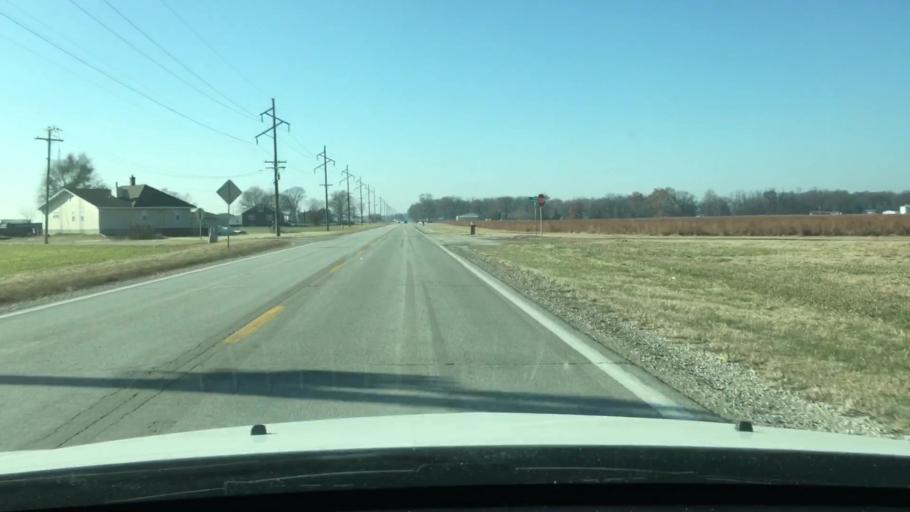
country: US
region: Illinois
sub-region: Cass County
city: Beardstown
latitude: 39.9879
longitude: -90.4417
